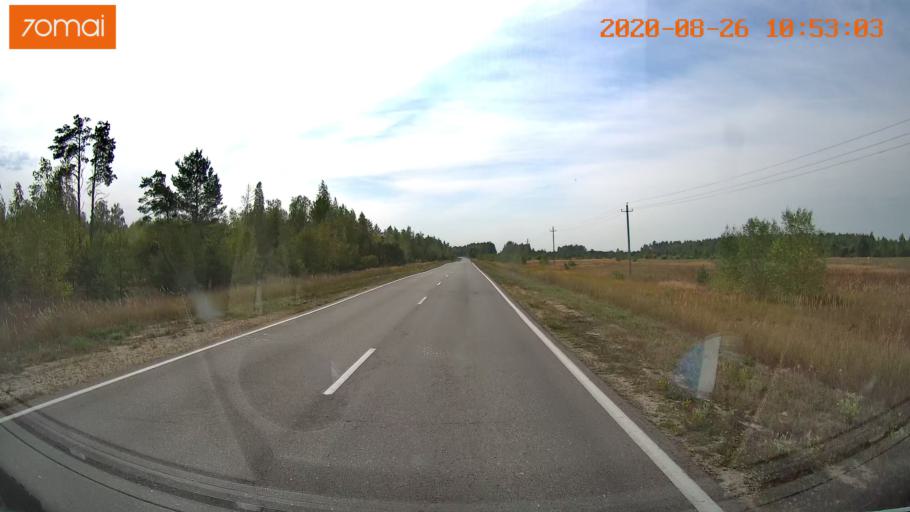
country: RU
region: Rjazan
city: Lashma
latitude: 54.6476
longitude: 41.1523
